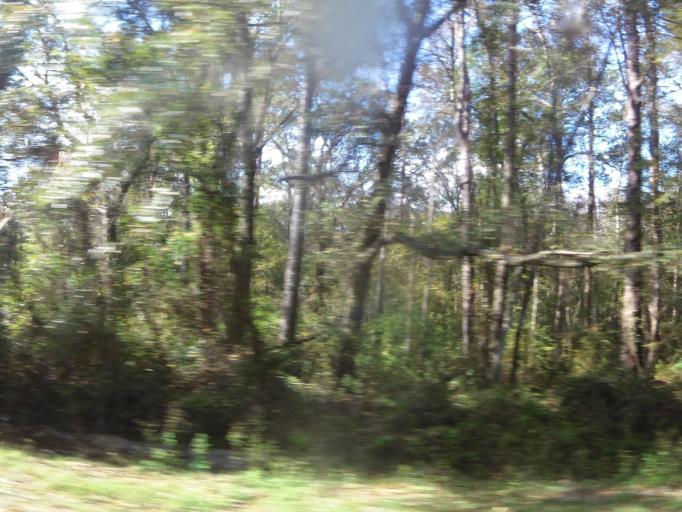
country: US
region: Florida
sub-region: Duval County
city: Baldwin
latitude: 30.1789
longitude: -81.9918
